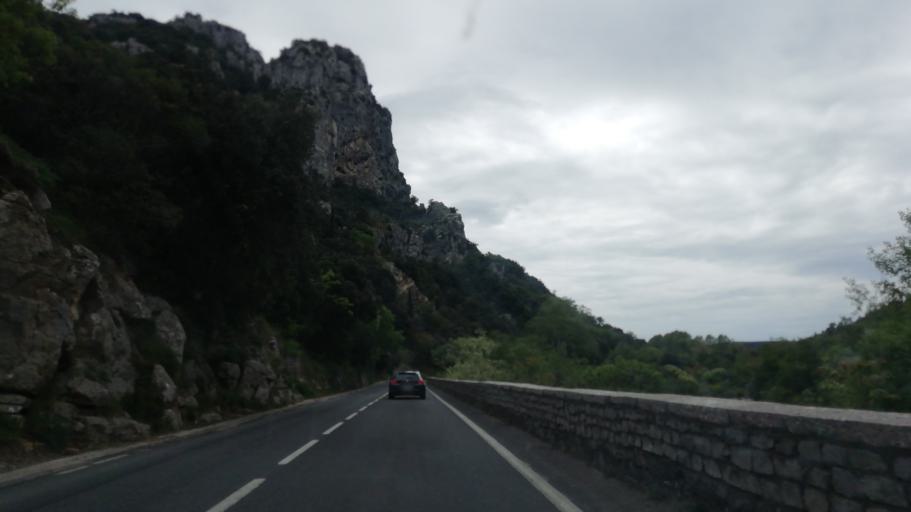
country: FR
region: Languedoc-Roussillon
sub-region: Departement de l'Herault
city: Saint-Bauzille-de-Putois
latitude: 43.9096
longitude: 3.7369
